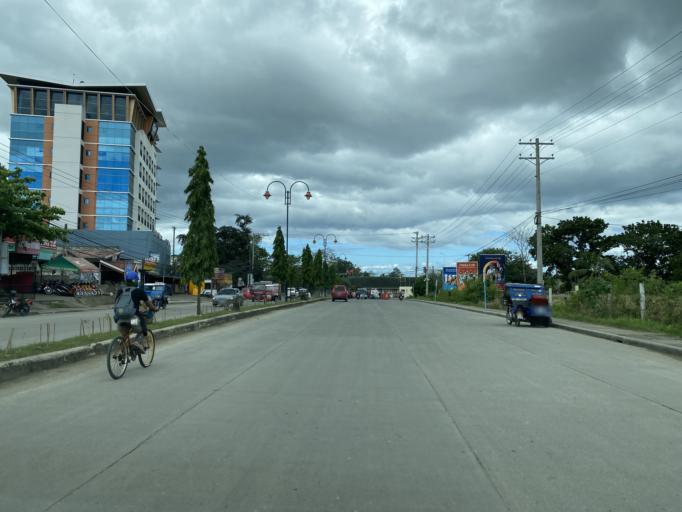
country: PH
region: Central Visayas
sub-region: Province of Bohol
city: Tagbilaran City
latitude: 9.6547
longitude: 123.8679
